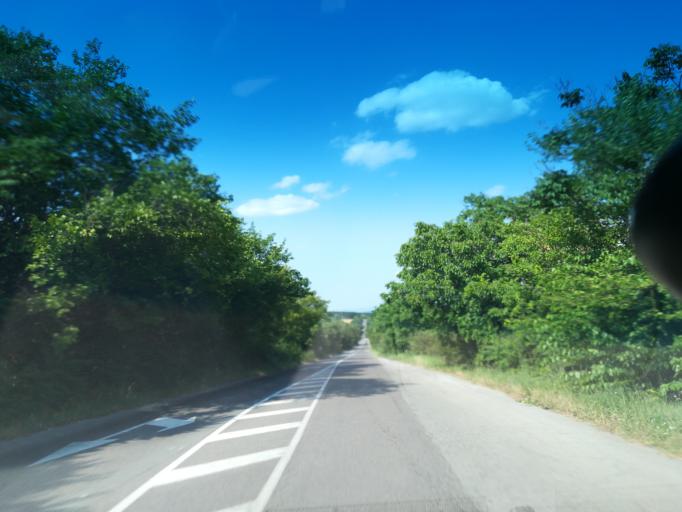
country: BG
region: Stara Zagora
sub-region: Obshtina Chirpan
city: Chirpan
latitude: 42.2210
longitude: 25.3850
